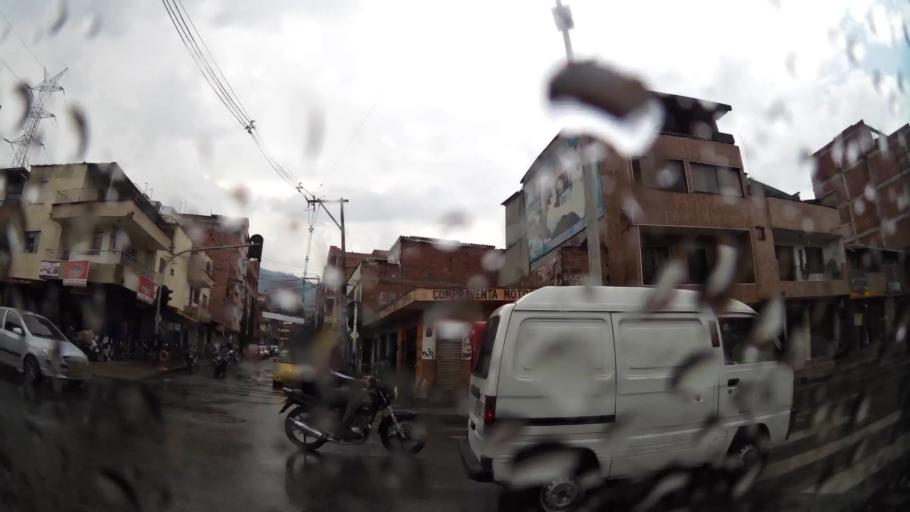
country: CO
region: Antioquia
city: Itagui
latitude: 6.1821
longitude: -75.5990
